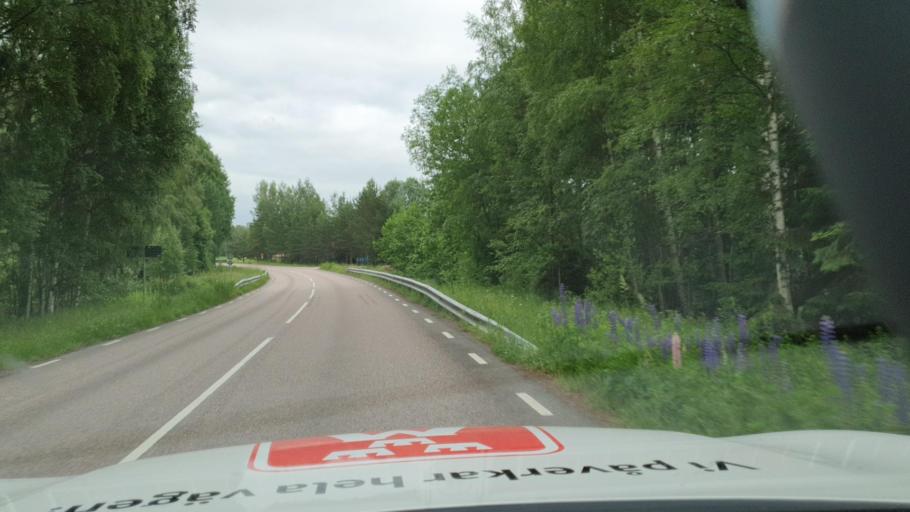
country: SE
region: Vaermland
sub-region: Kils Kommun
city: Kil
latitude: 59.5037
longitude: 13.3944
